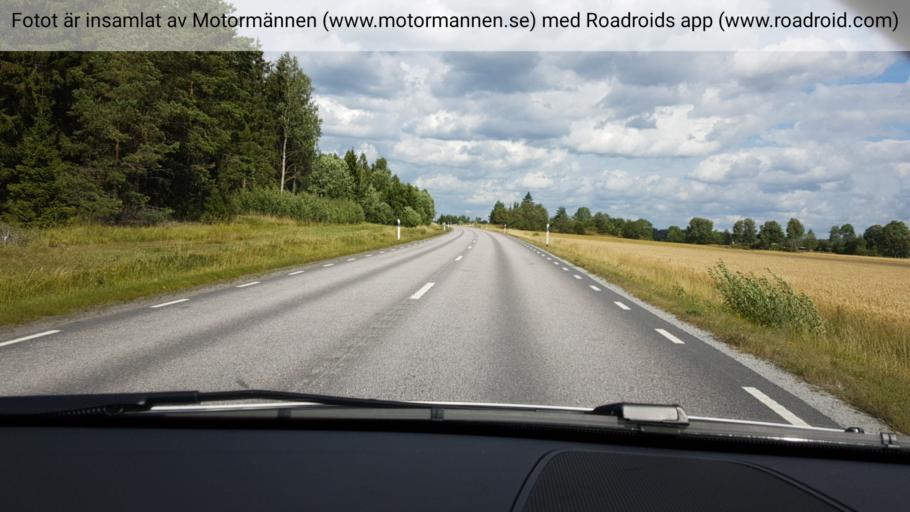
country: SE
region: Stockholm
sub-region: Vallentuna Kommun
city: Vallentuna
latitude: 59.7337
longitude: 18.0563
